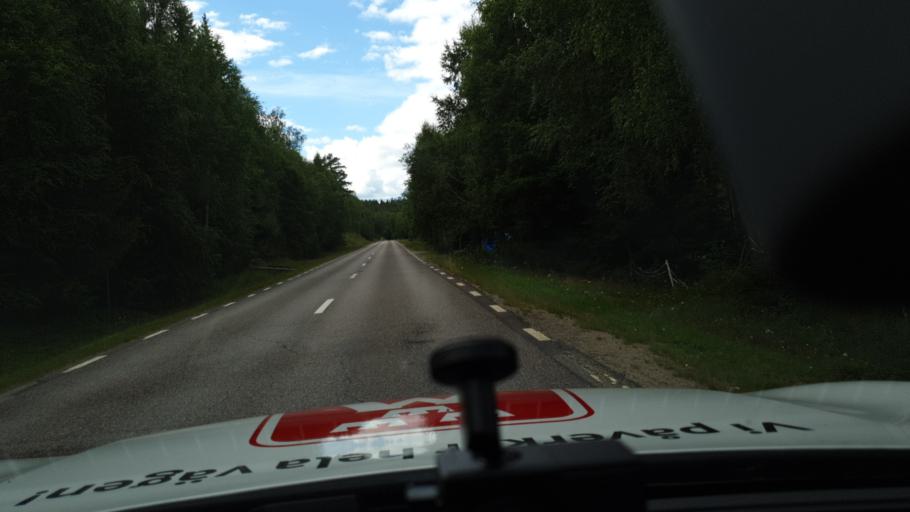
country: NO
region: Hedmark
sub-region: Trysil
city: Innbygda
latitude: 60.8984
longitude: 12.5890
